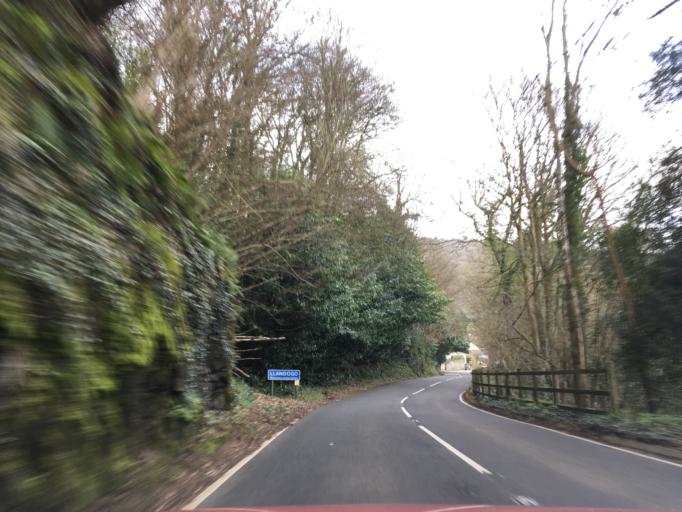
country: GB
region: Wales
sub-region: Monmouthshire
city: Tintern
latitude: 51.7290
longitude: -2.6884
